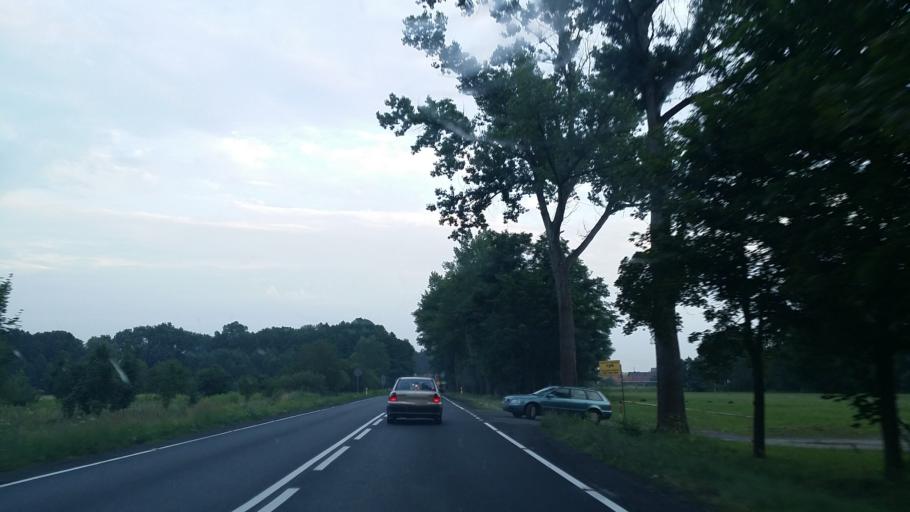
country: PL
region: Lower Silesian Voivodeship
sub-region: Powiat lubinski
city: Osiek
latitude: 51.3732
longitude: 16.2366
